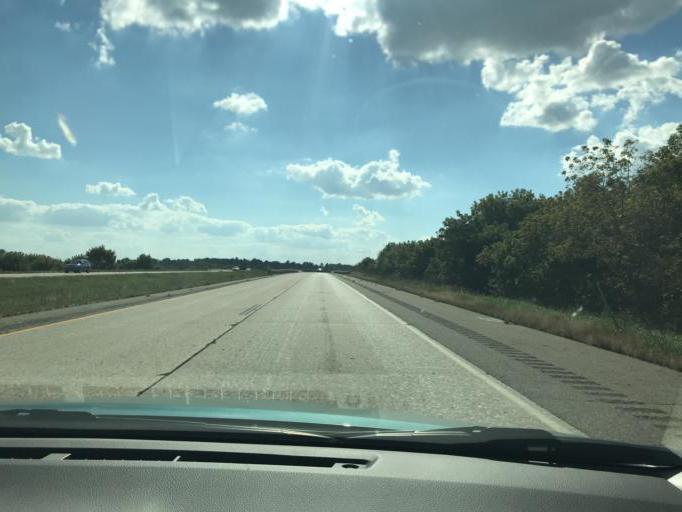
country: US
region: Wisconsin
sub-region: Walworth County
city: Darien
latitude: 42.5902
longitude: -88.7518
